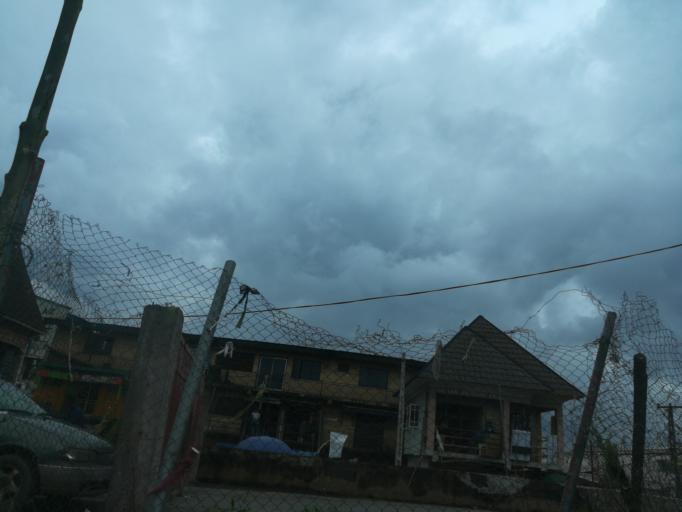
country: NG
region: Lagos
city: Agege
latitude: 6.6089
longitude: 3.3106
